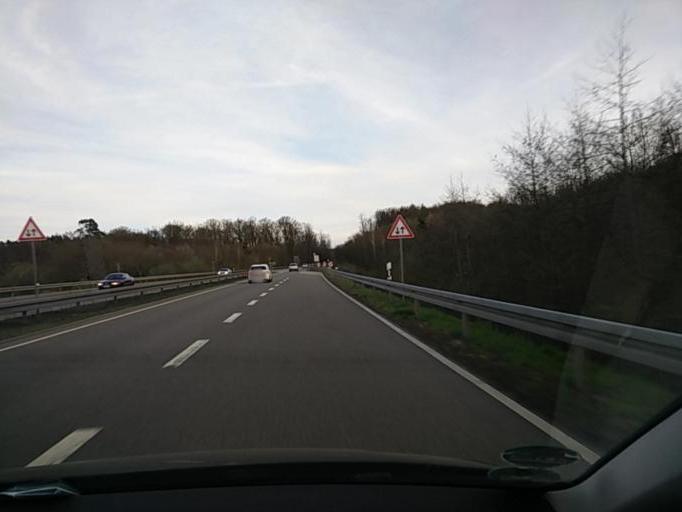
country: DE
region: Baden-Wuerttemberg
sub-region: Regierungsbezirk Stuttgart
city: Boeblingen
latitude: 48.6727
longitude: 8.9810
